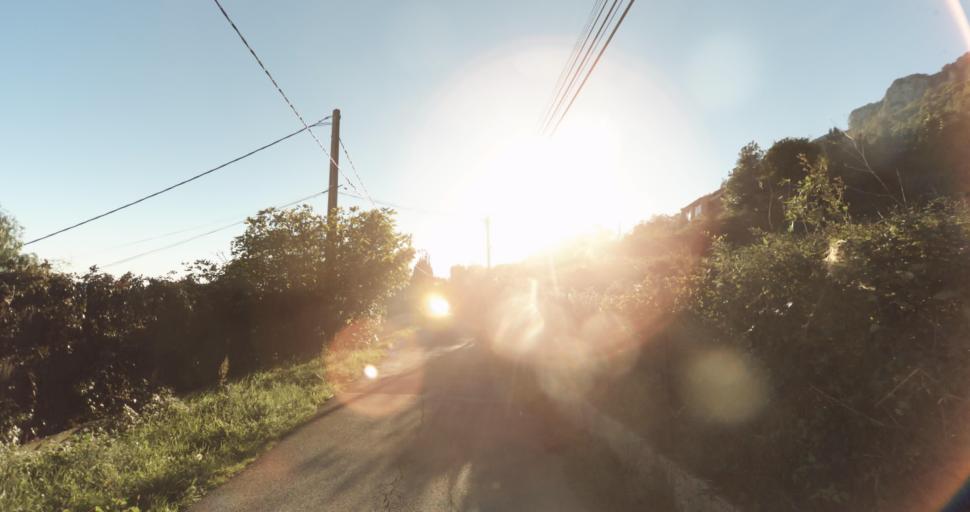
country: FR
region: Provence-Alpes-Cote d'Azur
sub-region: Departement des Alpes-Maritimes
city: Vence
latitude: 43.7373
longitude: 7.1207
